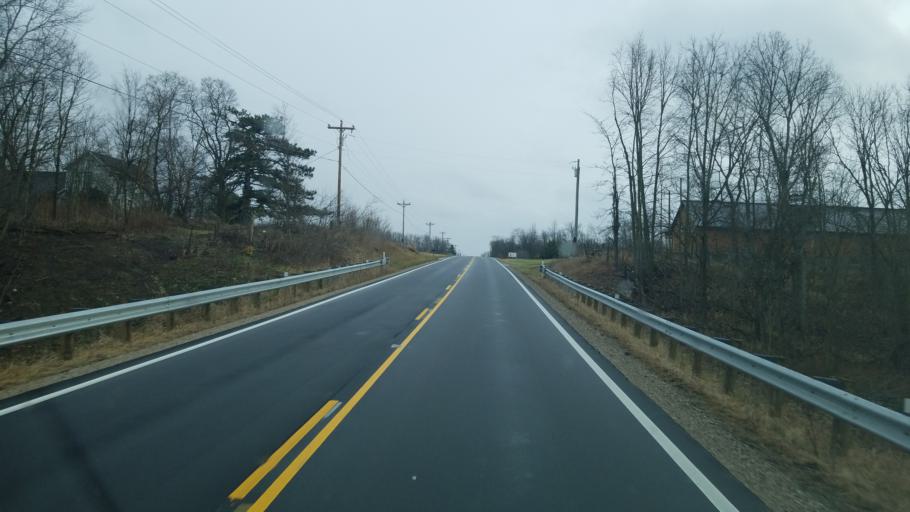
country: US
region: Ohio
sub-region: Union County
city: Richwood
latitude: 40.3817
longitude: -83.4054
